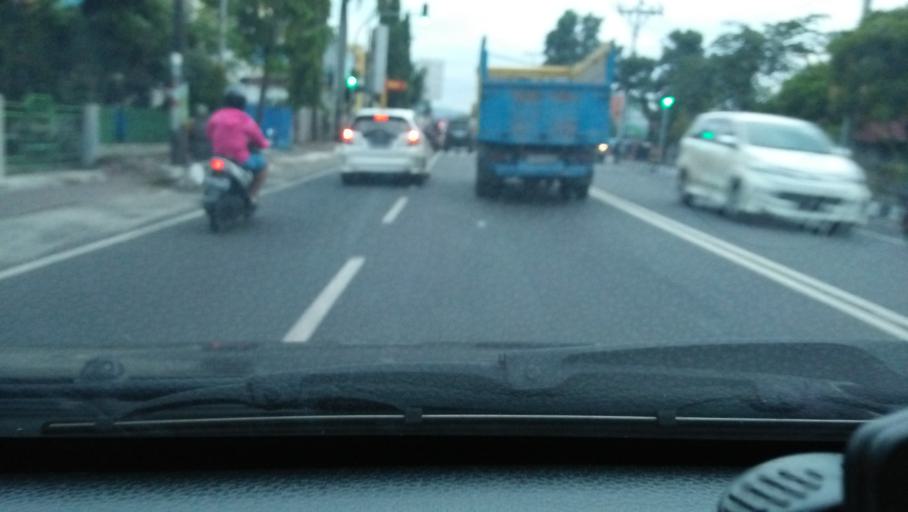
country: ID
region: Central Java
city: Magelang
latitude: -7.4570
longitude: 110.2230
